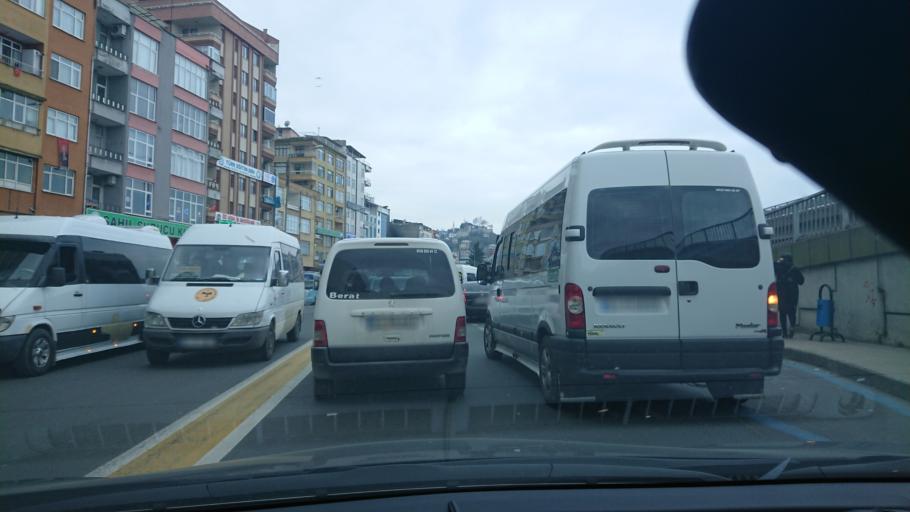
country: TR
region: Rize
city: Rize
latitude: 41.0257
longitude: 40.5223
